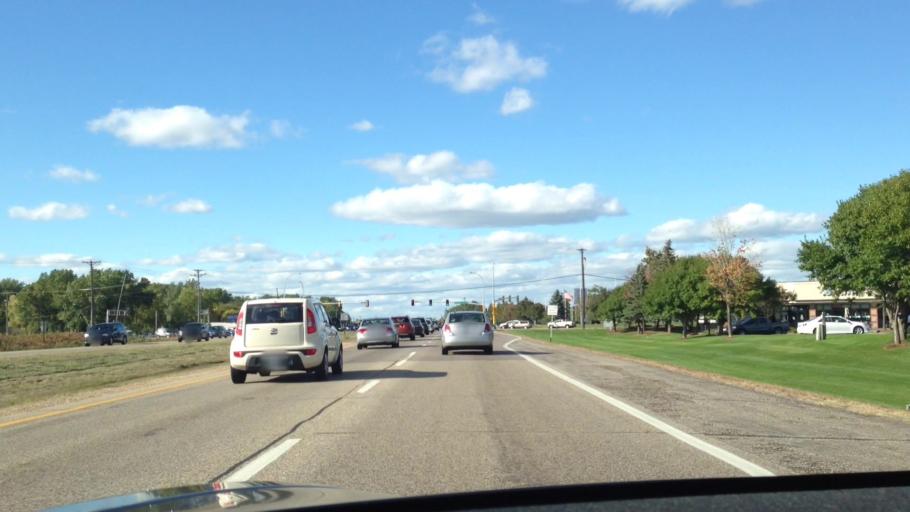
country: US
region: Minnesota
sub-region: Hennepin County
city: Brooklyn Park
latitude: 45.0936
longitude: -93.3835
